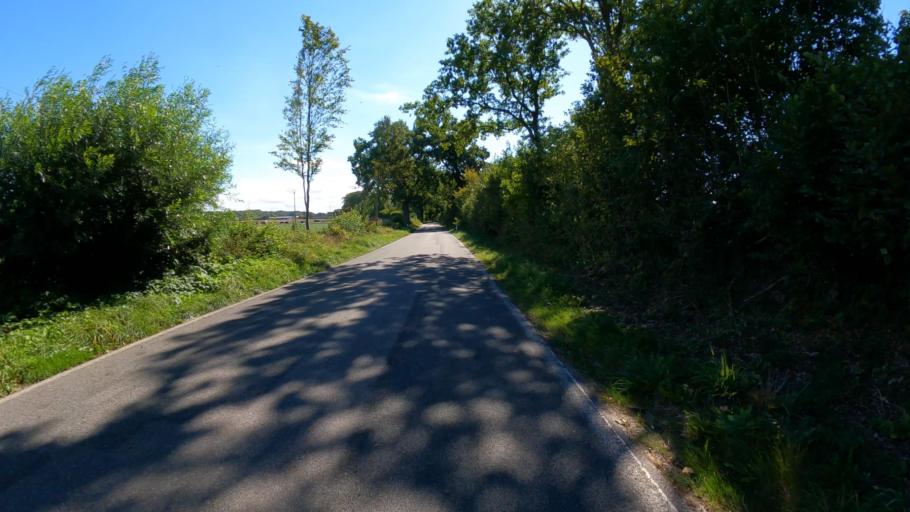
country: DE
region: Schleswig-Holstein
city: Westerau
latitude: 53.7772
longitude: 10.5212
